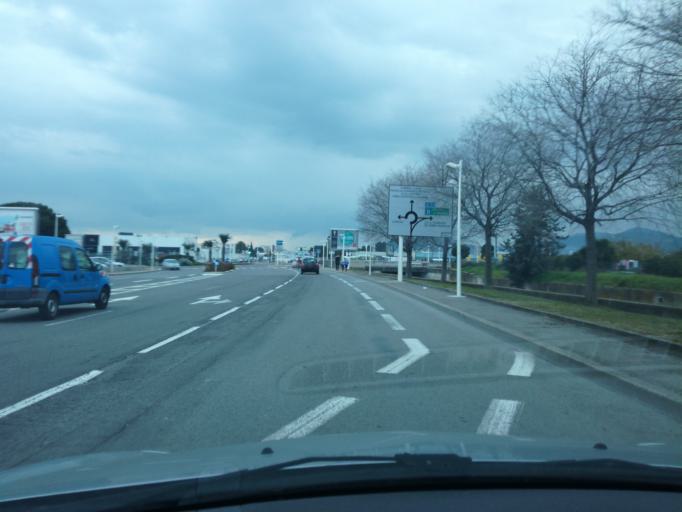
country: FR
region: Provence-Alpes-Cote d'Azur
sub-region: Departement des Alpes-Maritimes
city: Mandelieu-la-Napoule
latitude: 43.5513
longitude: 6.9622
